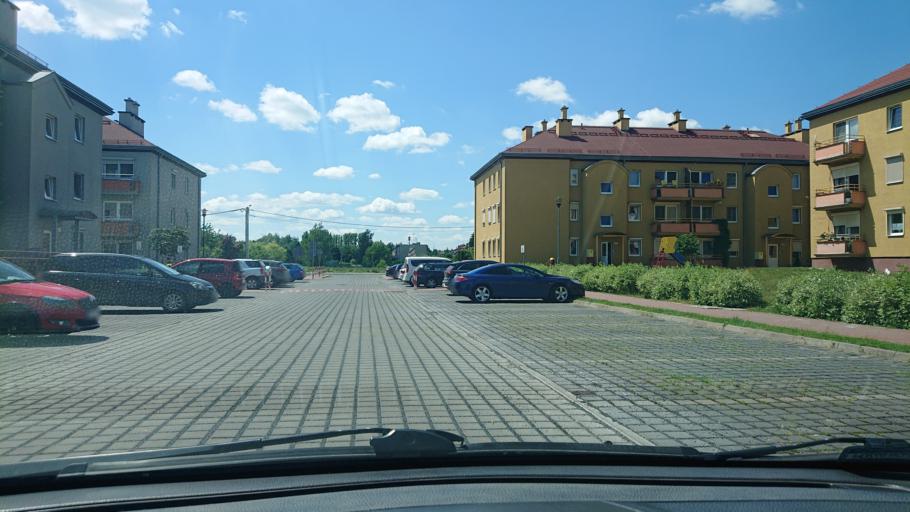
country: PL
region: Greater Poland Voivodeship
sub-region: Powiat gnieznienski
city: Gniezno
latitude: 52.5216
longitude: 17.6142
